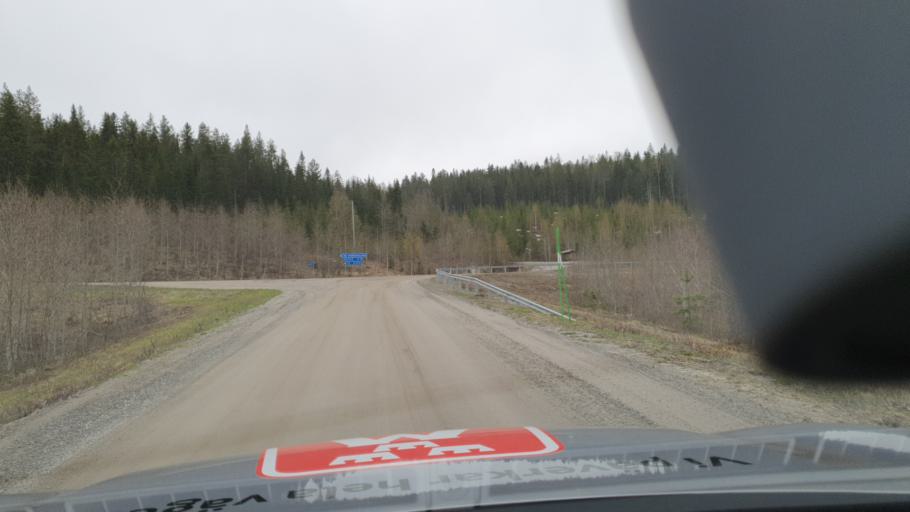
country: SE
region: Vaesternorrland
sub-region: OErnskoeldsviks Kommun
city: Husum
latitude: 63.6302
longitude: 19.0591
